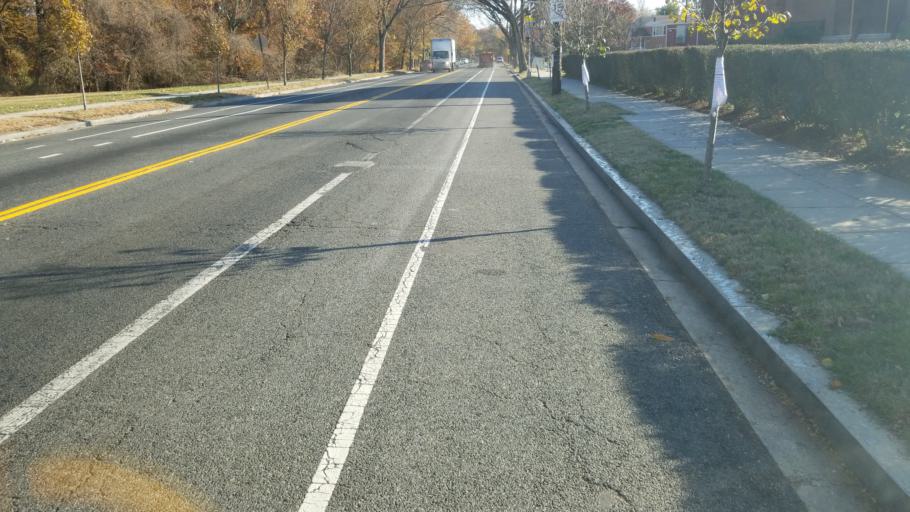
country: US
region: Maryland
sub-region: Prince George's County
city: Coral Hills
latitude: 38.8708
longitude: -76.9432
